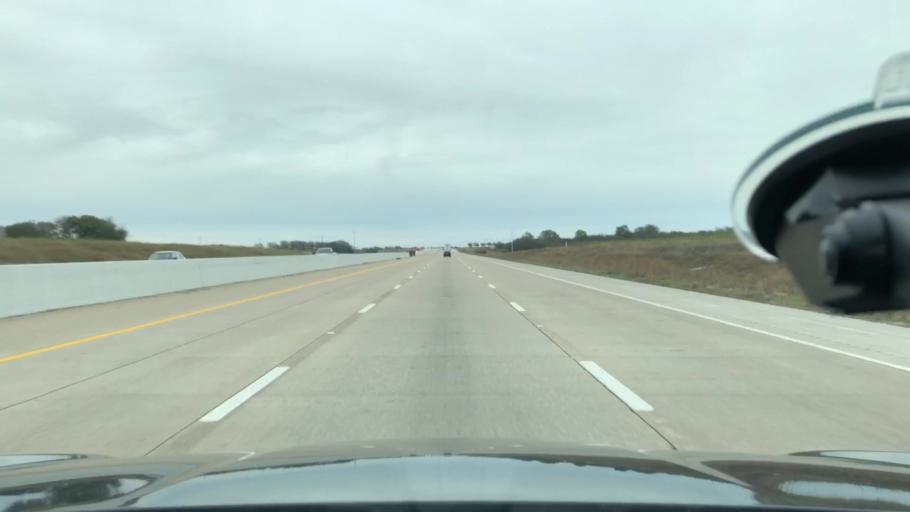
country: US
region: Texas
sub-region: Ellis County
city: Italy
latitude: 32.1541
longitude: -96.9289
